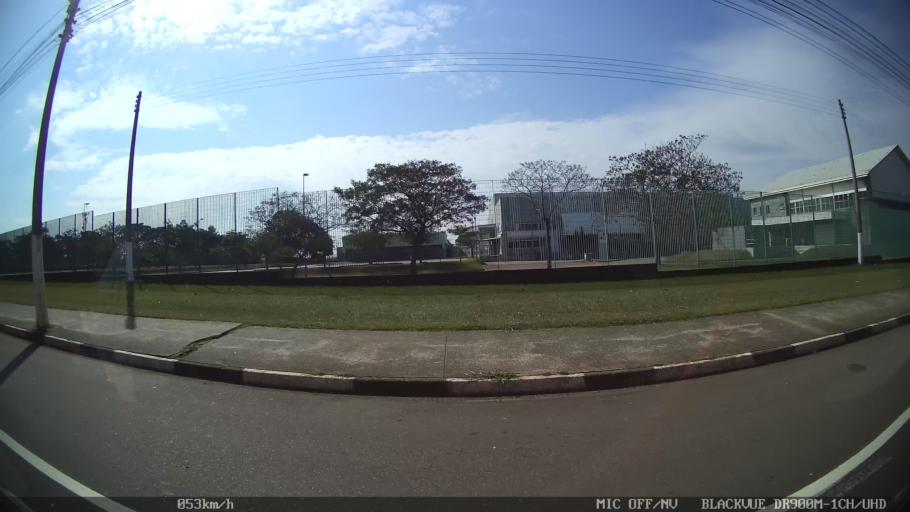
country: BR
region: Sao Paulo
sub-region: Paulinia
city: Paulinia
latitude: -22.7833
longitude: -47.1567
